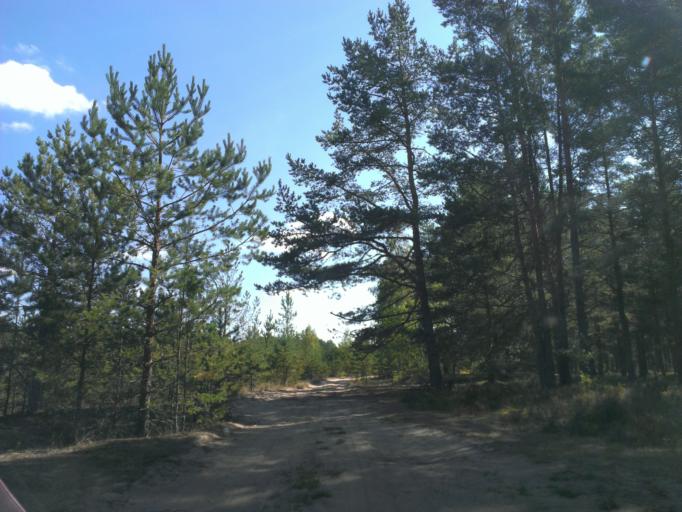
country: LV
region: Adazi
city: Adazi
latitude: 57.1096
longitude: 24.3469
